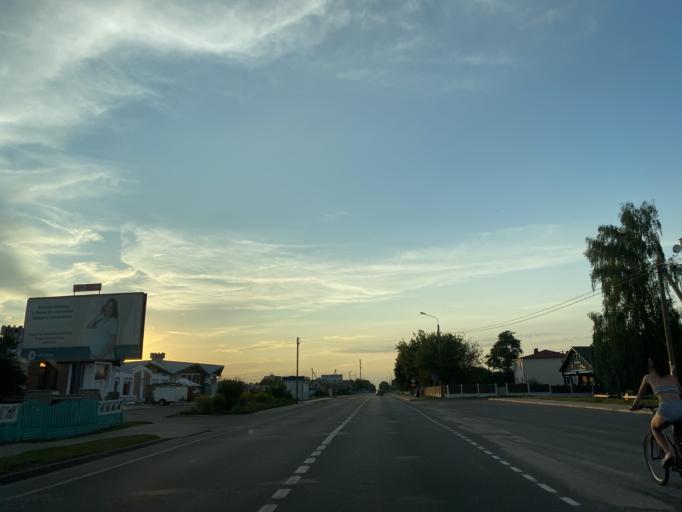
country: BY
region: Brest
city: Ivatsevichy
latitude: 52.7083
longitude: 25.3550
